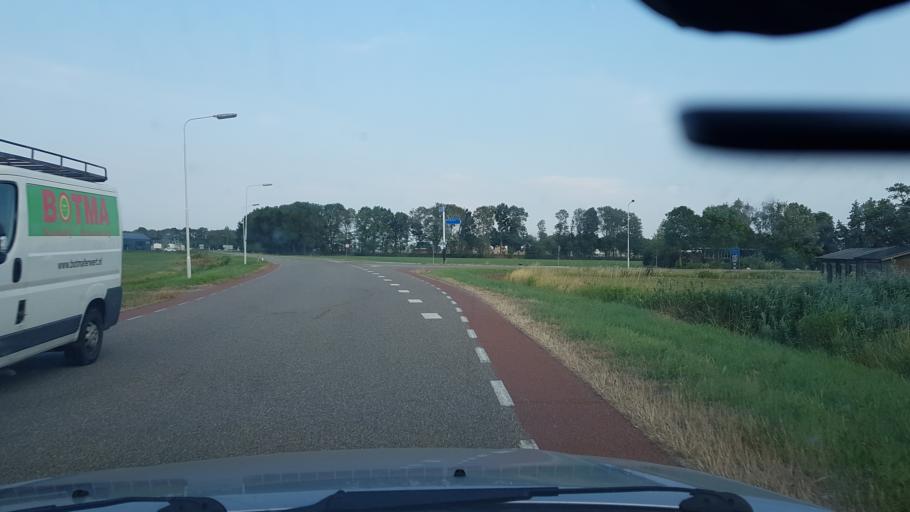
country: NL
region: Friesland
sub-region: Gemeente Ferwerderadiel
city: Burdaard
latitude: 53.2997
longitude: 5.8765
